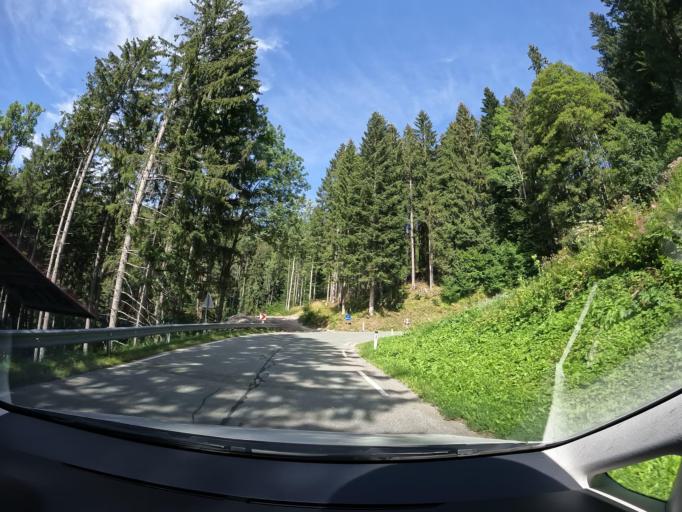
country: AT
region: Carinthia
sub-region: Politischer Bezirk Feldkirchen
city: Glanegg
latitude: 46.7491
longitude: 14.2163
